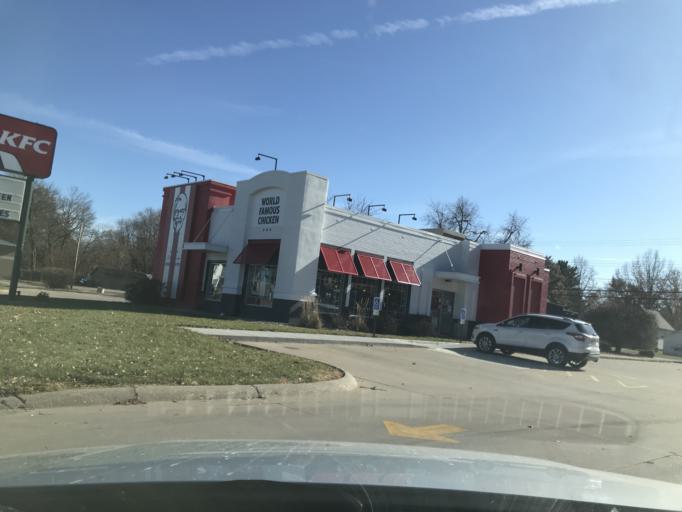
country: US
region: Illinois
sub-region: McDonough County
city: Macomb
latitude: 40.4586
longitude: -90.6643
